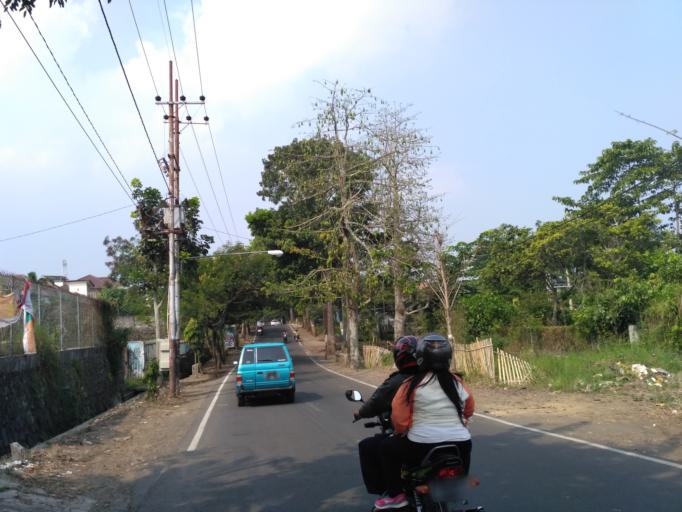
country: ID
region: East Java
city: Batu
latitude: -7.8633
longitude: 112.5325
